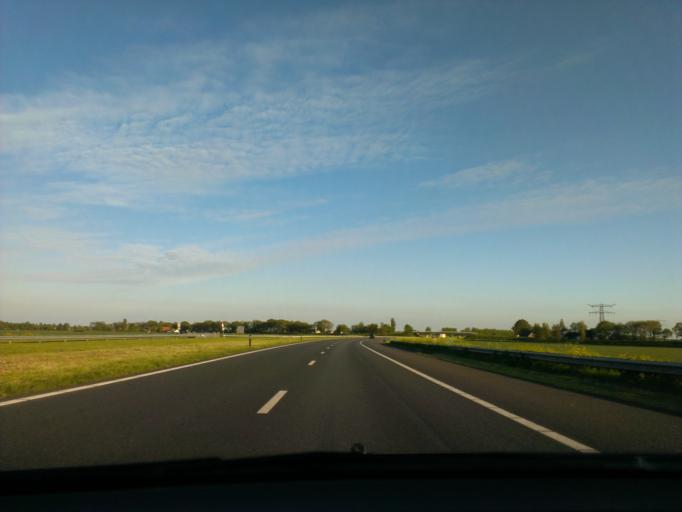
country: NL
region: South Holland
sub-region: Gemeente Oud-Beijerland
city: Oud-Beijerland
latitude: 51.7766
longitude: 4.4198
